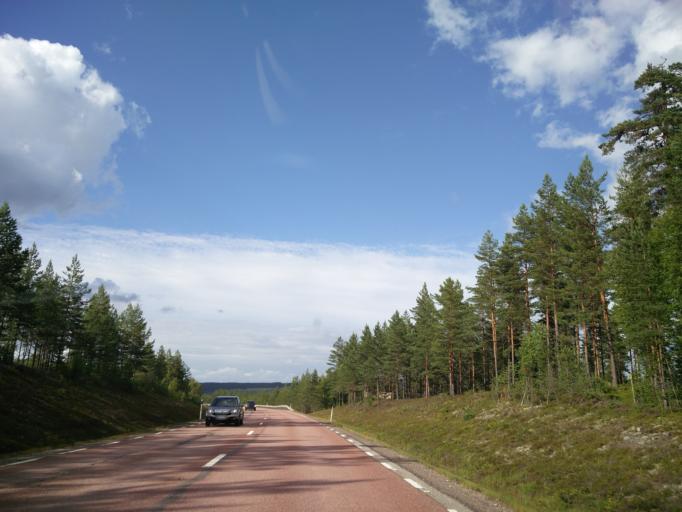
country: SE
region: Vaermland
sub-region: Hagfors Kommun
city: Ekshaerad
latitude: 60.3914
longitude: 13.2621
